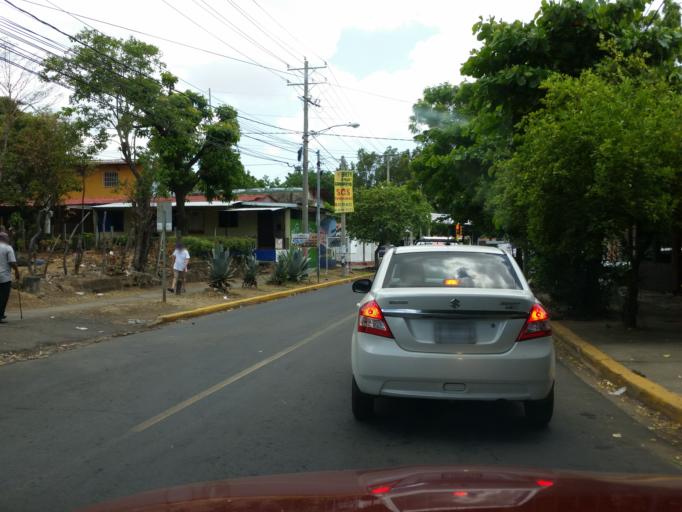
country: NI
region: Managua
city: Managua
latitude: 12.1151
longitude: -86.2521
